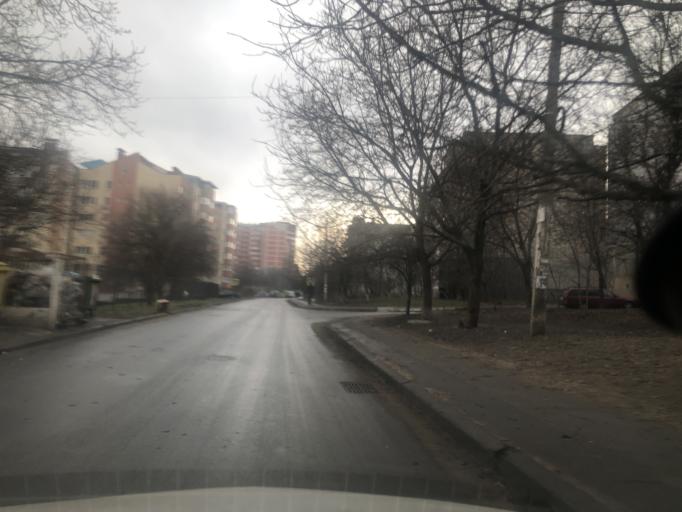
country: MD
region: Chisinau
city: Stauceni
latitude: 47.0649
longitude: 28.8425
